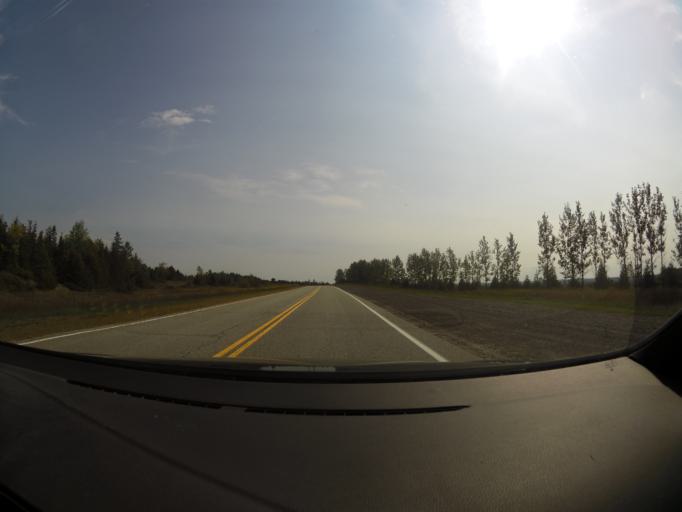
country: CA
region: Ontario
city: Arnprior
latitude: 45.3420
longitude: -76.1958
